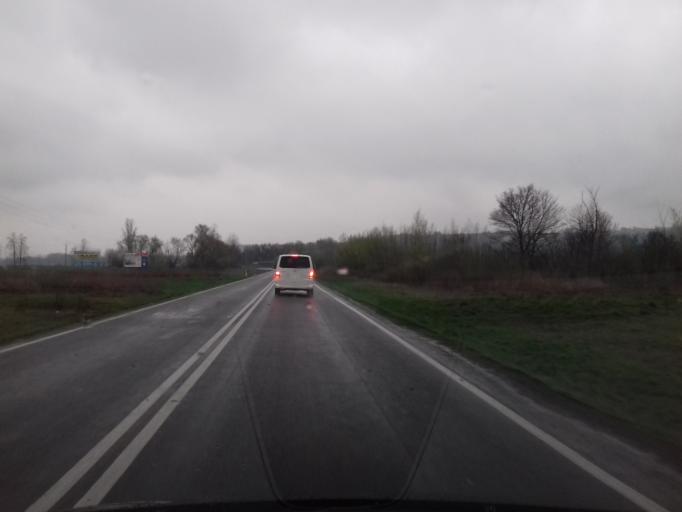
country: PL
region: Lesser Poland Voivodeship
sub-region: Powiat nowosadecki
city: Stary Sacz
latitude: 49.5488
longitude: 20.6526
